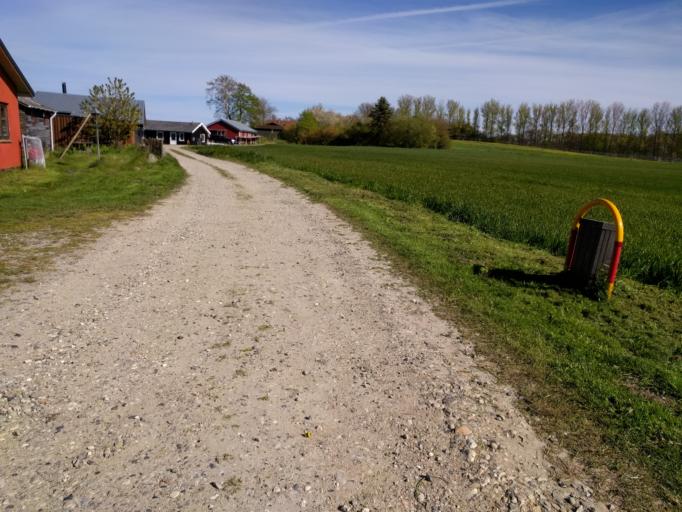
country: DK
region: South Denmark
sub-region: Kerteminde Kommune
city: Munkebo
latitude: 55.4388
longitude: 10.5493
